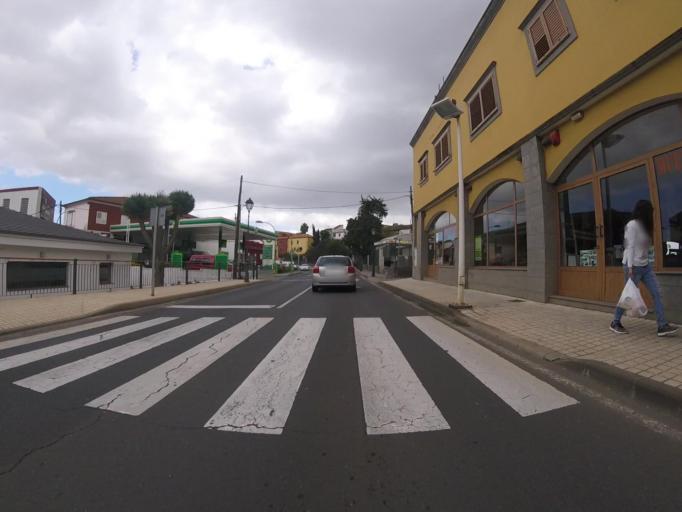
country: ES
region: Canary Islands
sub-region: Provincia de Las Palmas
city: Vega de San Mateo
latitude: 28.0089
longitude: -15.5361
